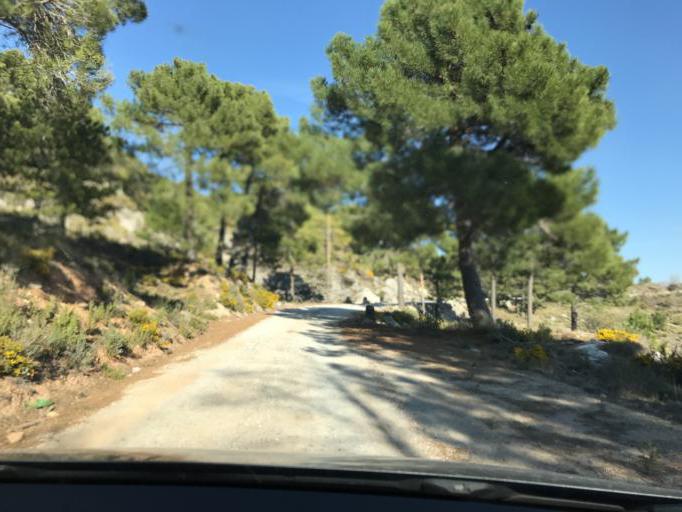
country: ES
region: Andalusia
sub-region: Provincia de Granada
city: Beas de Granada
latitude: 37.2423
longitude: -3.4516
